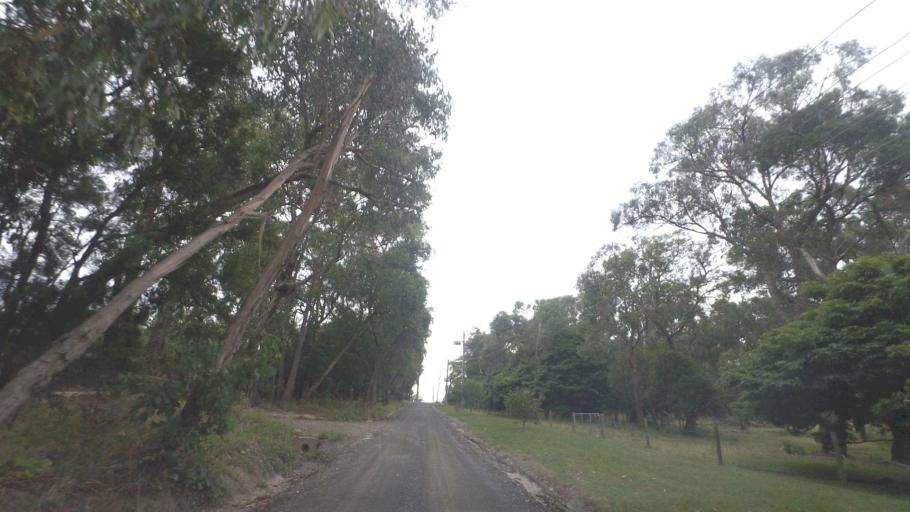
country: AU
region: Victoria
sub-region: Yarra Ranges
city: Mount Evelyn
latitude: -37.7628
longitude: 145.3753
